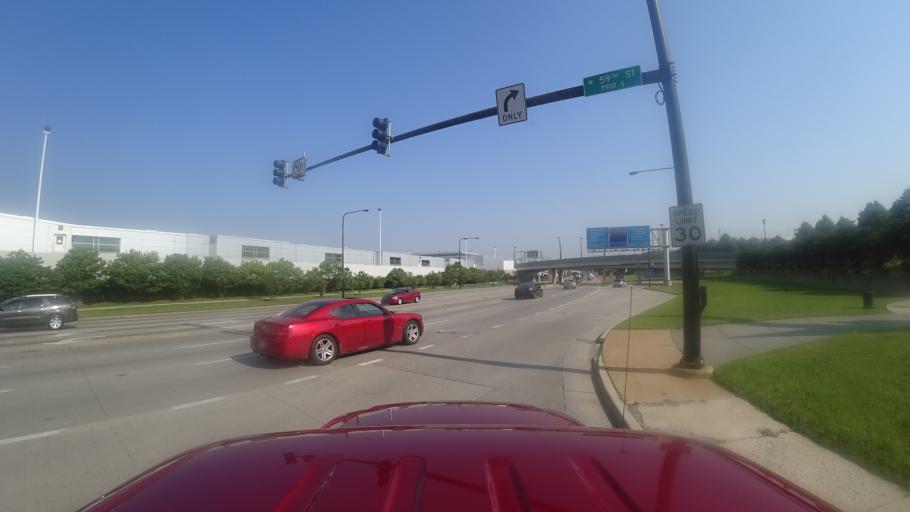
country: US
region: Illinois
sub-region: Cook County
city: Hometown
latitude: 41.7845
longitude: -87.7411
